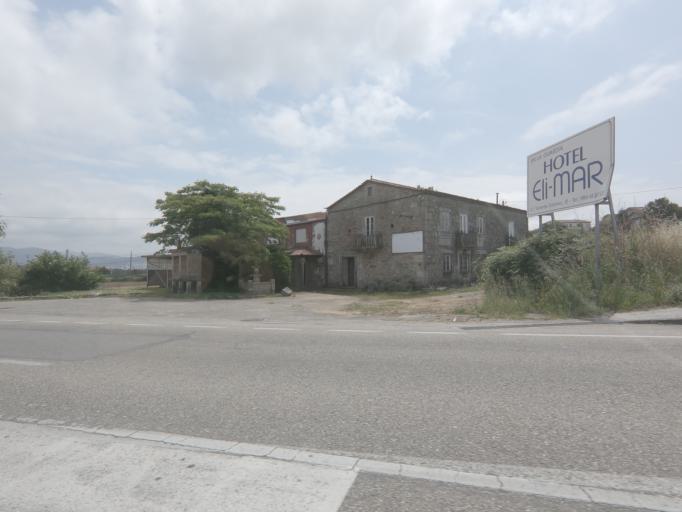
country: ES
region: Galicia
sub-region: Provincia de Pontevedra
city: A Guarda
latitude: 41.9092
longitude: -8.8583
